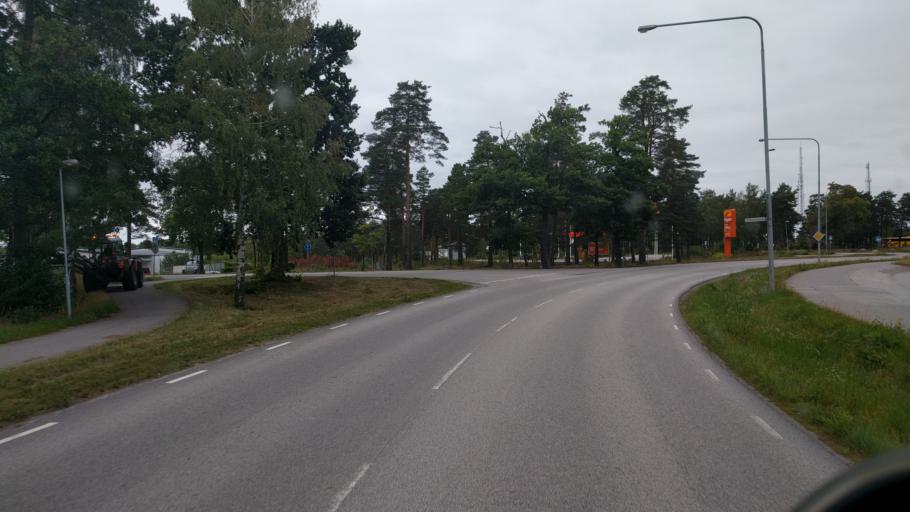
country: SE
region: Kalmar
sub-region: Vasterviks Kommun
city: Vaestervik
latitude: 57.7637
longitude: 16.5993
